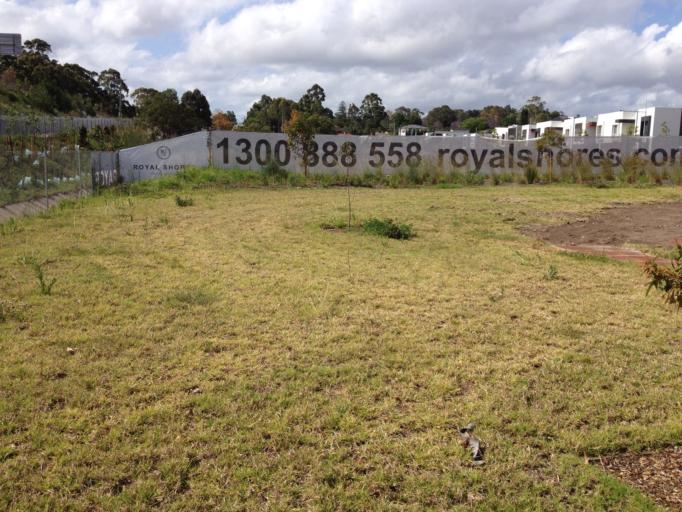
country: AU
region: New South Wales
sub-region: Parramatta
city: Ermington
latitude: -33.8233
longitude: 151.0518
